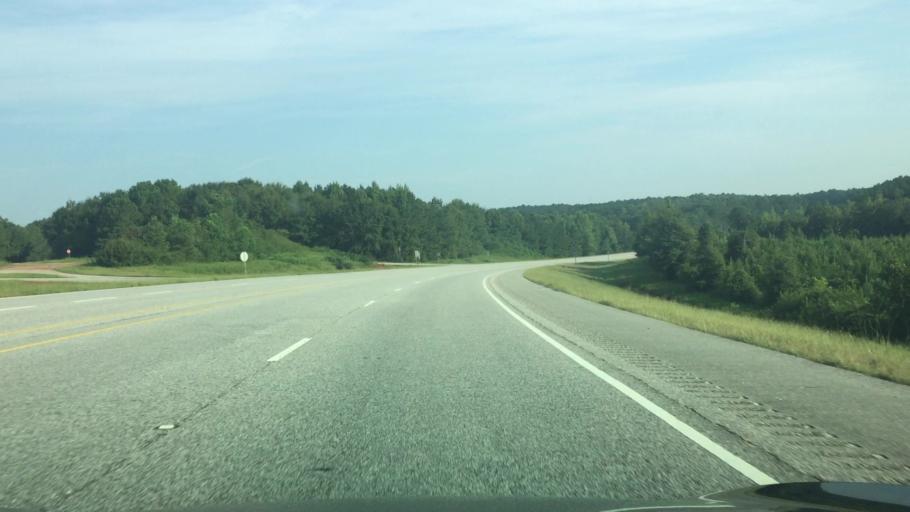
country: US
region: Alabama
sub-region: Butler County
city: Georgiana
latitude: 31.5044
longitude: -86.7004
